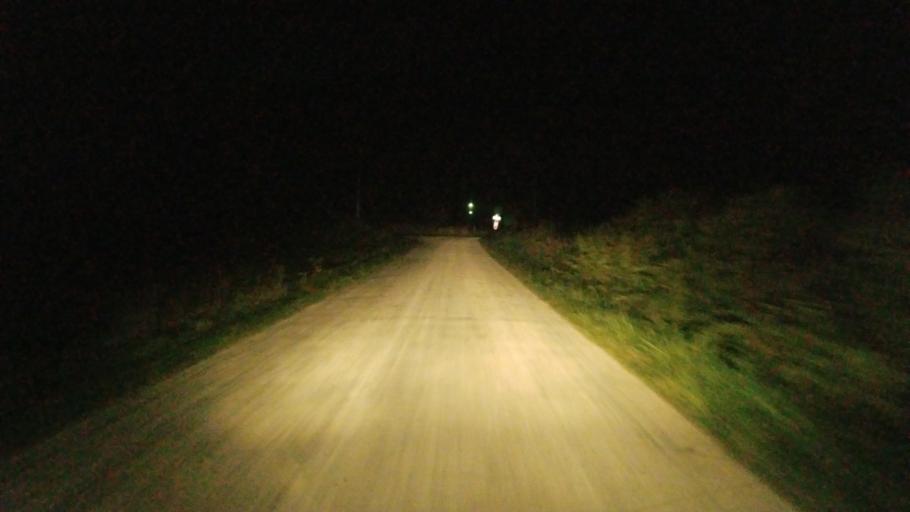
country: US
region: Ohio
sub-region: Ashland County
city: Ashland
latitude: 40.9014
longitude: -82.4066
